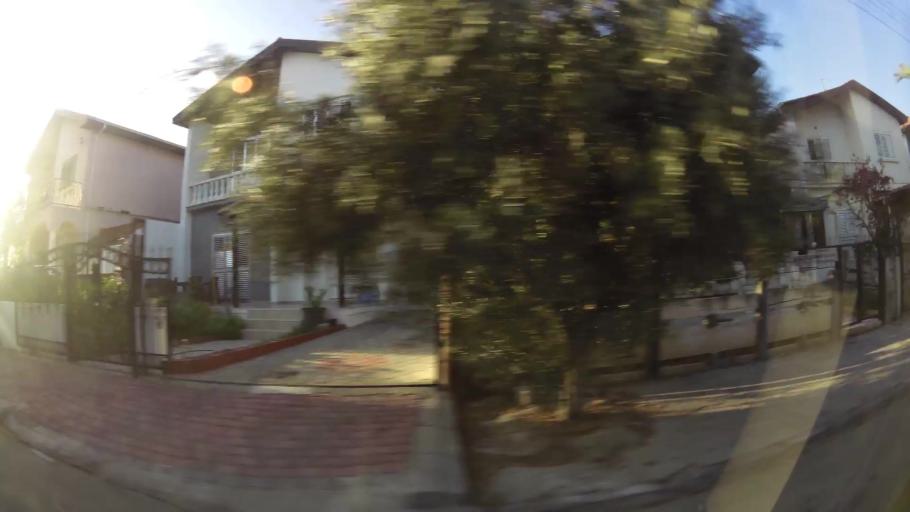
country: CY
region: Lefkosia
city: Nicosia
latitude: 35.2041
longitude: 33.3086
